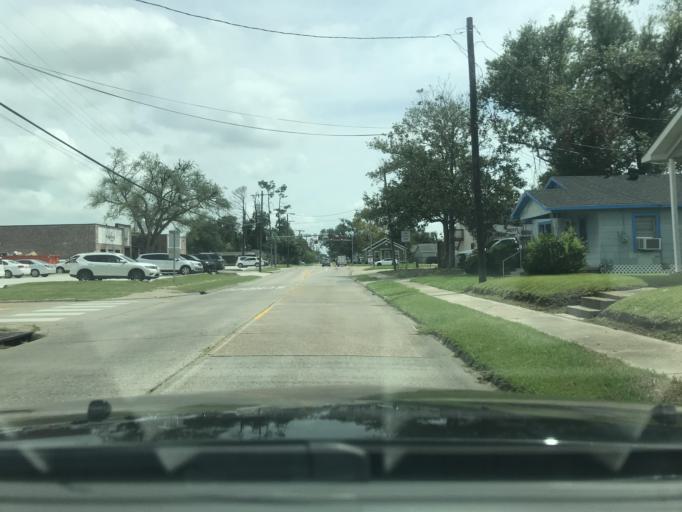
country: US
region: Louisiana
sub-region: Calcasieu Parish
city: Lake Charles
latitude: 30.2044
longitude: -93.2141
